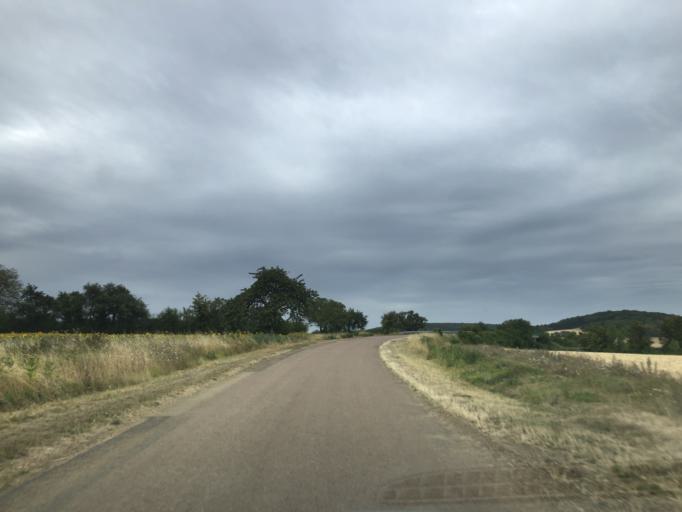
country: FR
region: Bourgogne
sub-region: Departement de l'Yonne
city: Aillant-sur-Tholon
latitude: 47.9085
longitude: 3.3425
